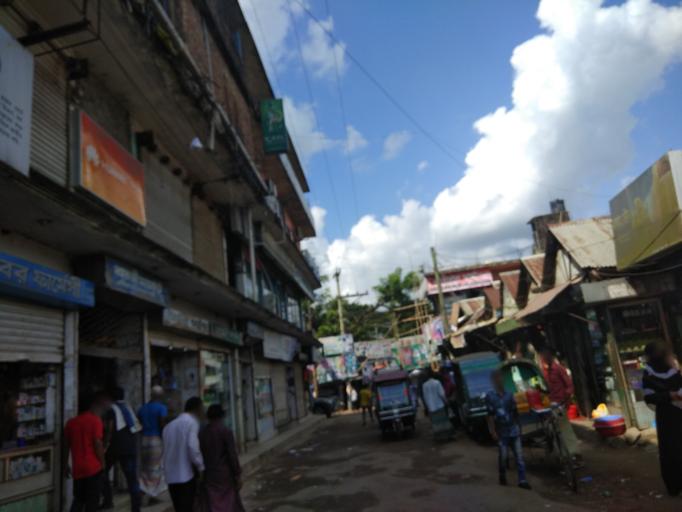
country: BD
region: Dhaka
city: Narayanganj
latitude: 23.5101
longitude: 90.4663
